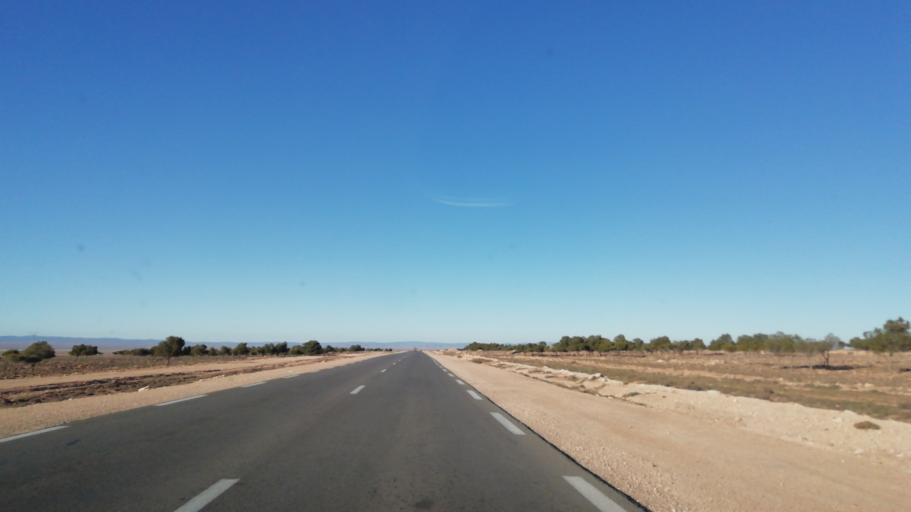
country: DZ
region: Tlemcen
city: Sebdou
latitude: 34.2839
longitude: -1.2593
